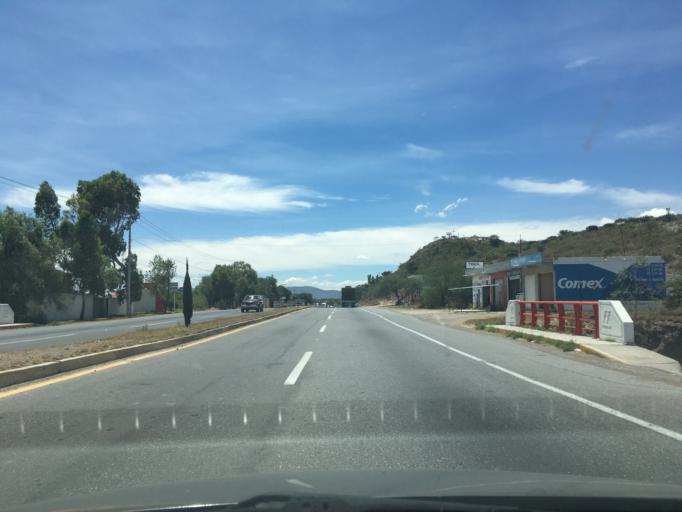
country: MX
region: Hidalgo
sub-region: Tasquillo
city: Portezuelo
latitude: 20.4833
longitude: -99.2904
